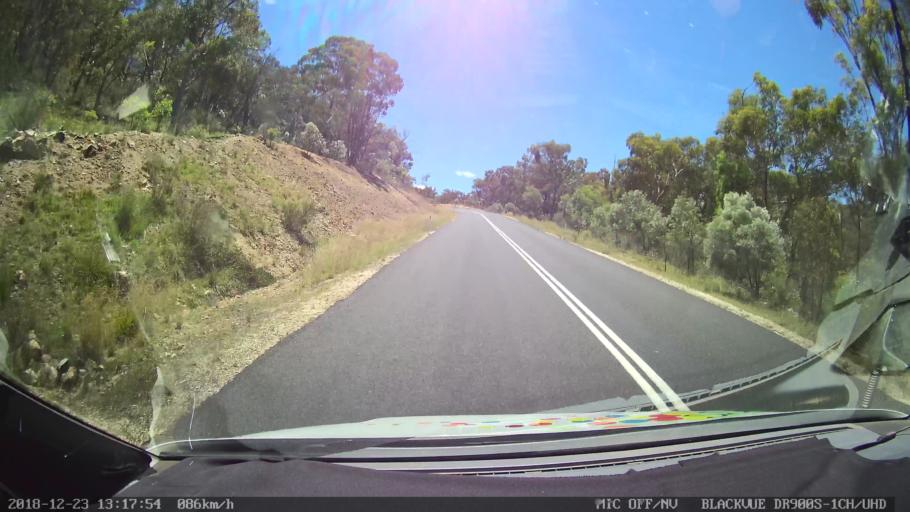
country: AU
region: New South Wales
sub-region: Armidale Dumaresq
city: Armidale
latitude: -30.4885
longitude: 151.4819
